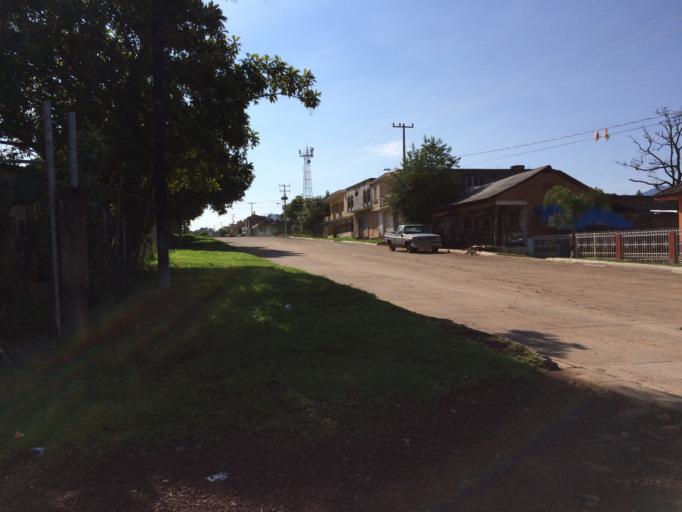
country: MX
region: Michoacan
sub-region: Uruapan
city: Nuevo Zirosto
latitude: 19.5478
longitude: -102.3502
